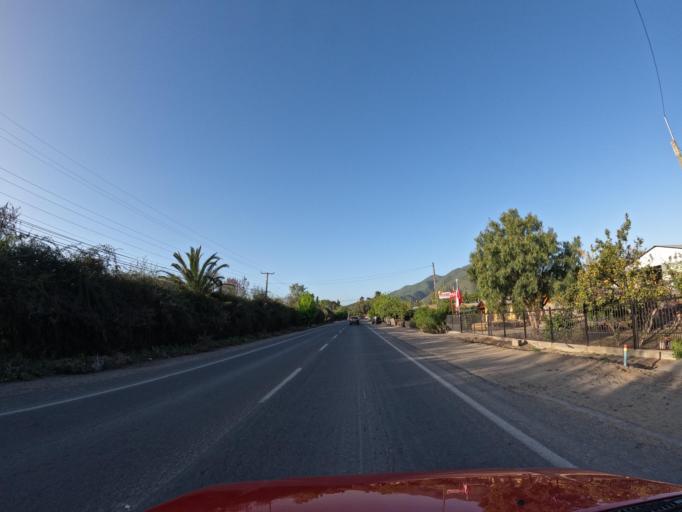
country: CL
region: O'Higgins
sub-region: Provincia de Colchagua
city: Santa Cruz
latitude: -34.4036
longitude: -71.3703
